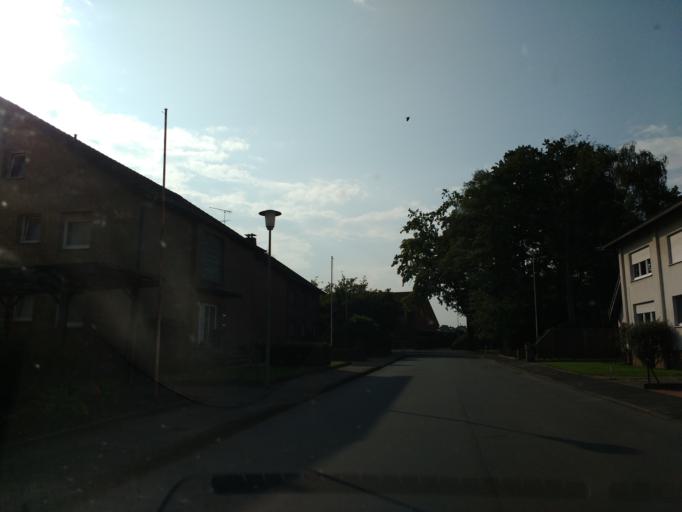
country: DE
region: North Rhine-Westphalia
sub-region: Regierungsbezirk Detmold
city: Hovelhof
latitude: 51.7613
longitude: 8.6513
